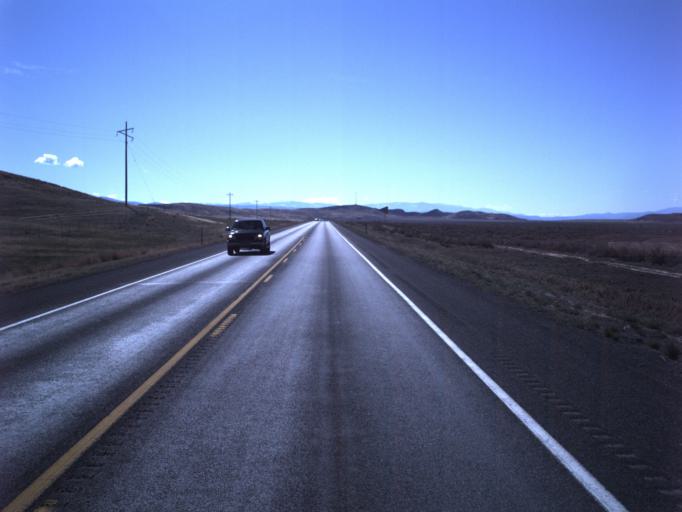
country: US
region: Utah
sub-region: Sanpete County
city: Gunnison
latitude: 39.2049
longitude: -111.8477
